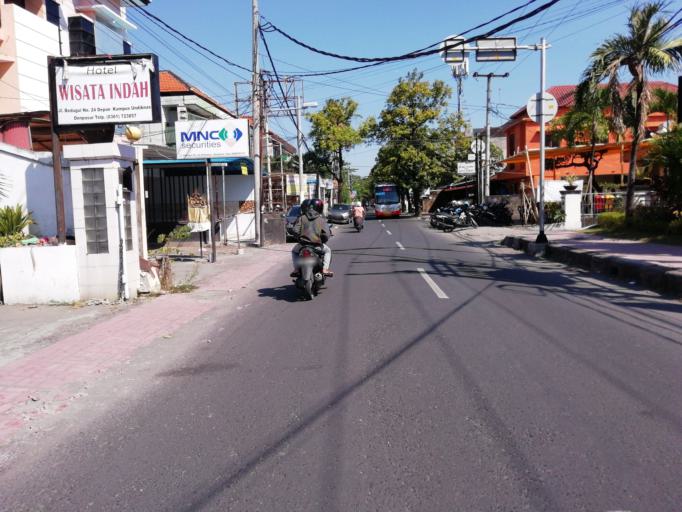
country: ID
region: Bali
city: Karyadharma
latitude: -8.6968
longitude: 115.2271
